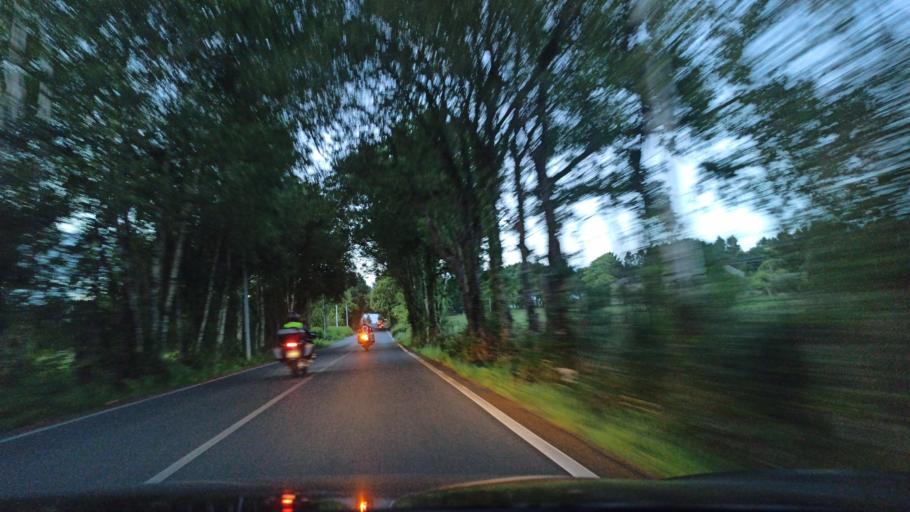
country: ES
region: Galicia
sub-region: Provincia de Lugo
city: Lugo
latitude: 42.9829
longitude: -7.5842
